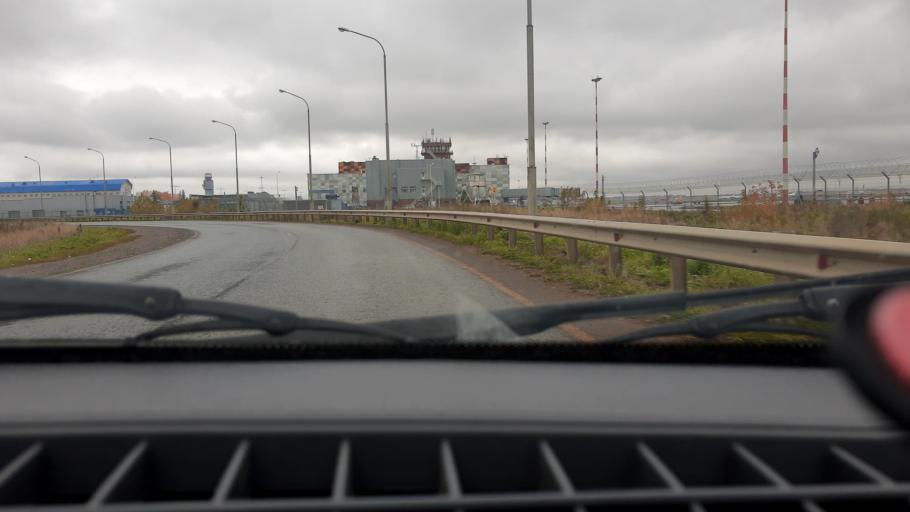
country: RU
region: Bashkortostan
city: Avdon
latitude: 54.5690
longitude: 55.8800
